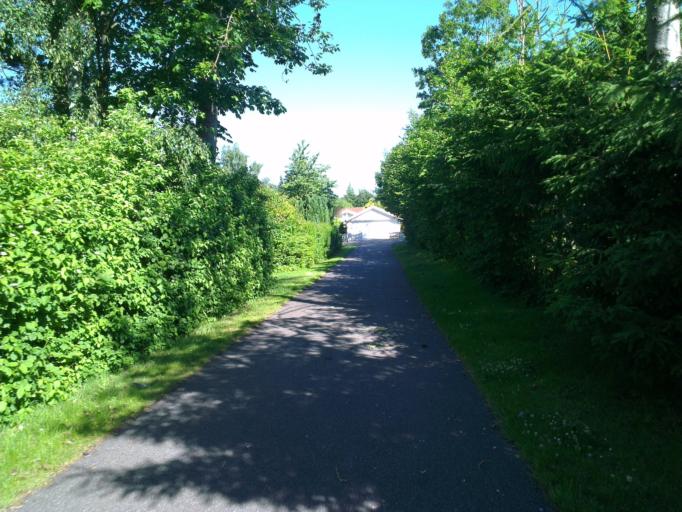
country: DK
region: Capital Region
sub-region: Halsnaes Kommune
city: Hundested
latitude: 55.9168
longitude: 11.9120
